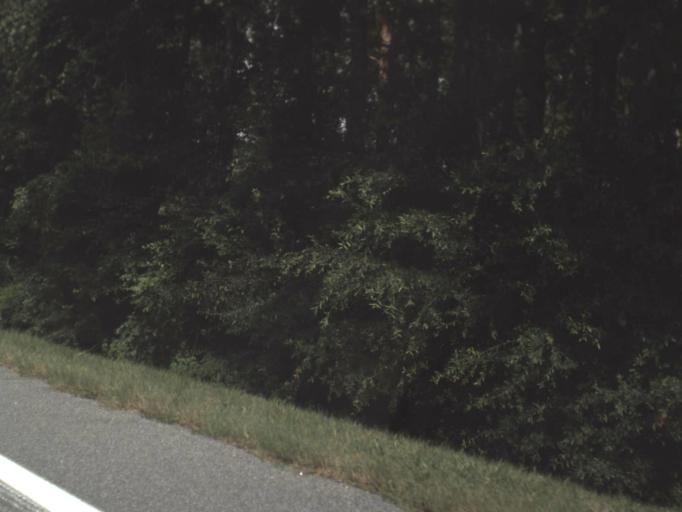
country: US
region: Florida
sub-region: Union County
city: Lake Butler
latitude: 30.0465
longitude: -82.3031
